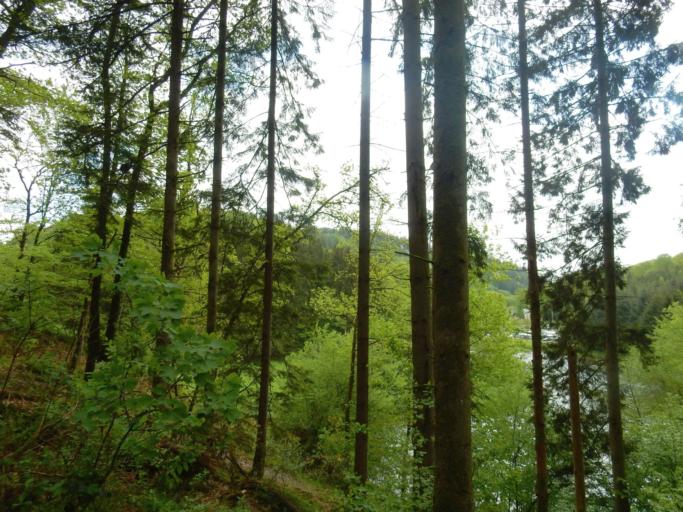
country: BE
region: Wallonia
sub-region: Province du Luxembourg
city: Bouillon
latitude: 49.7920
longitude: 5.0406
